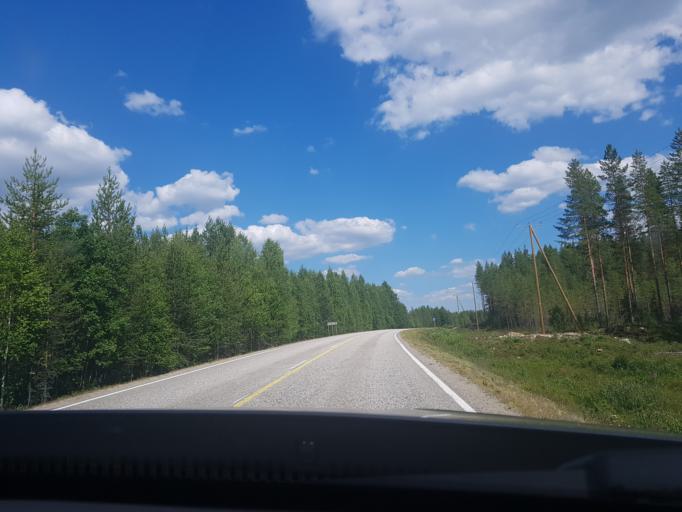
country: FI
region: Kainuu
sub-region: Kehys-Kainuu
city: Kuhmo
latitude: 64.2249
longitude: 29.8050
